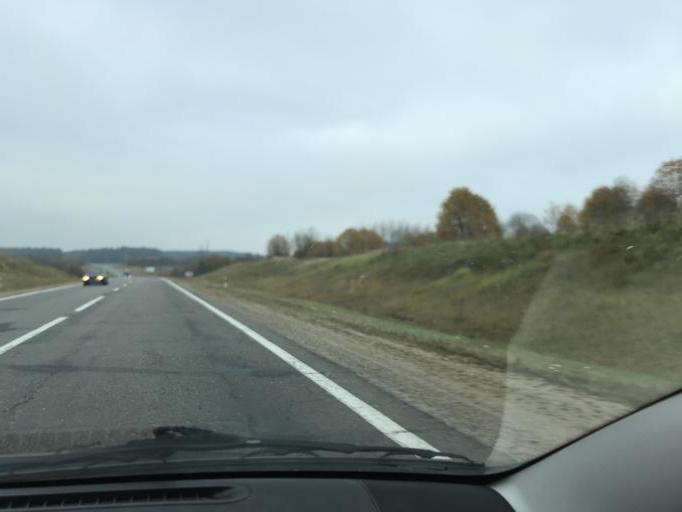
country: BY
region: Vitebsk
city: Syanno
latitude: 55.0432
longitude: 29.5131
